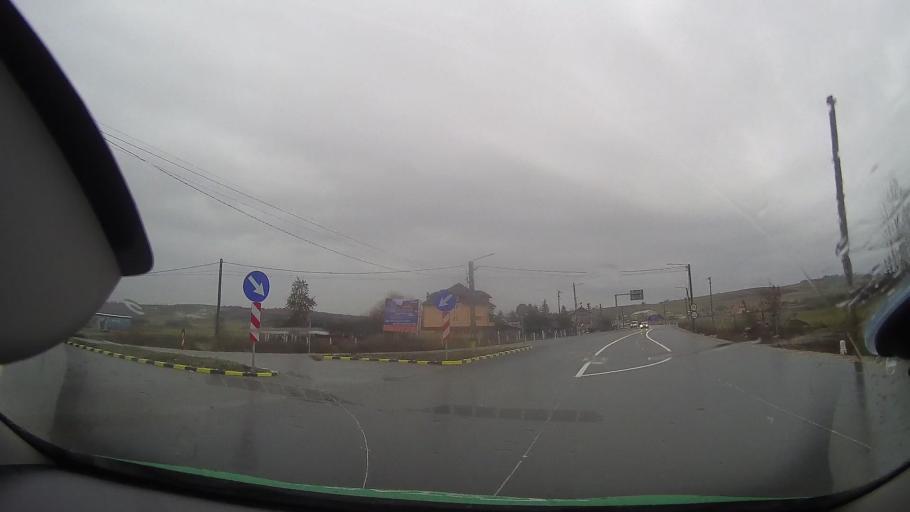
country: RO
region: Bihor
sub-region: Comuna Pocola
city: Pocola
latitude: 46.6986
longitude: 22.2870
